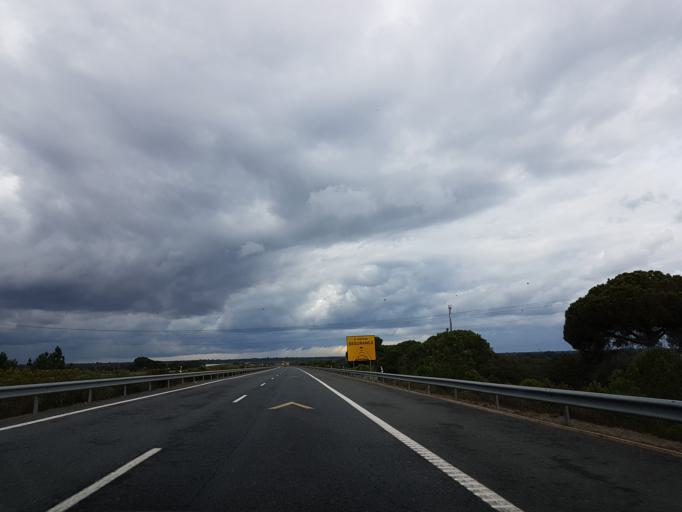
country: PT
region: Beja
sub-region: Aljustrel
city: Aljustrel
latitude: 38.0394
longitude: -8.2986
